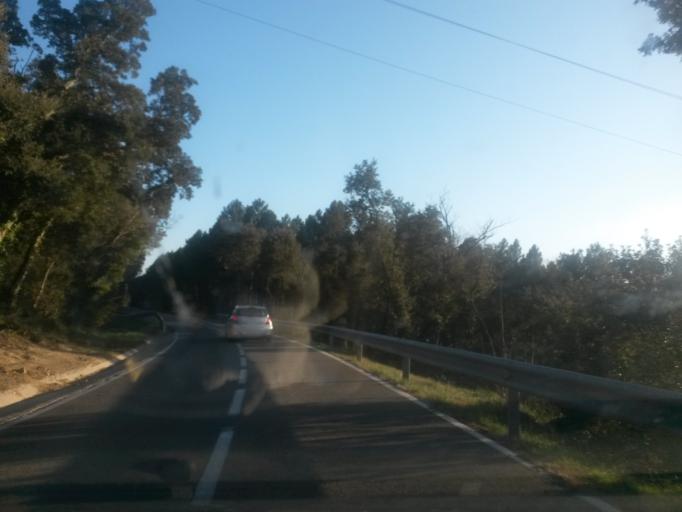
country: ES
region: Catalonia
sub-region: Provincia de Girona
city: Macanet de Cabrenys
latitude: 42.3827
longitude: 2.7876
